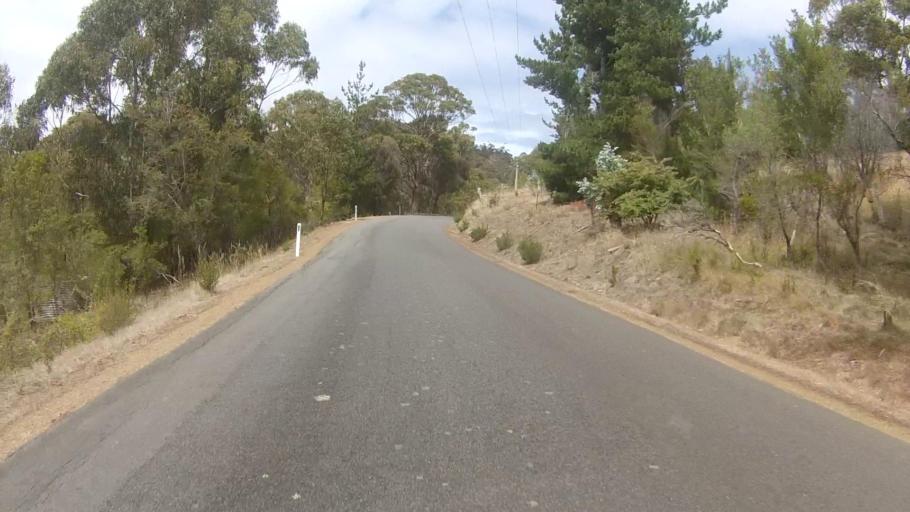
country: AU
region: Tasmania
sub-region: Kingborough
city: Blackmans Bay
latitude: -43.0422
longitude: 147.3359
